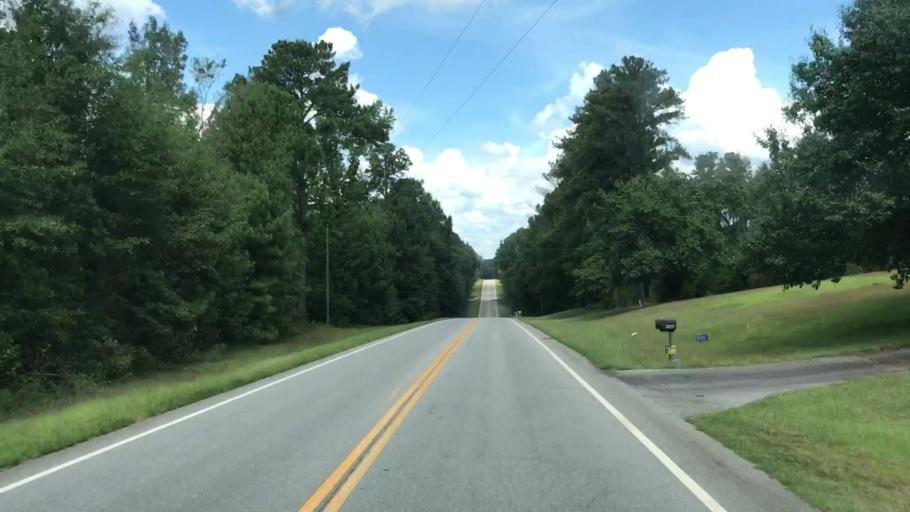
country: US
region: Georgia
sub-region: Greene County
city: Greensboro
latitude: 33.6216
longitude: -83.2123
